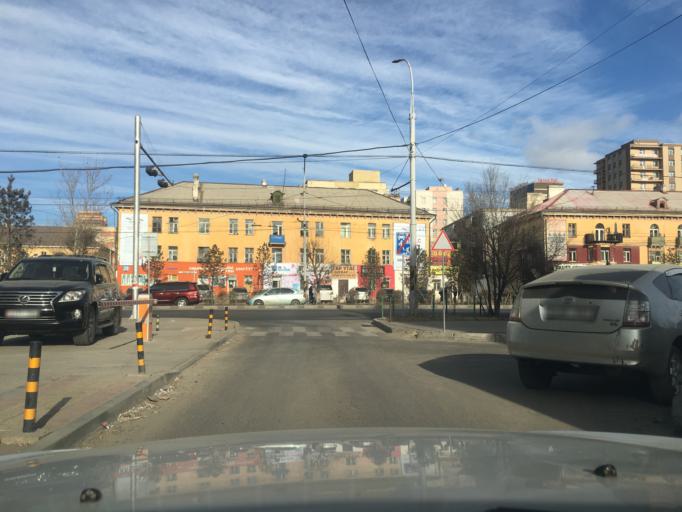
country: MN
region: Ulaanbaatar
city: Ulaanbaatar
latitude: 47.9142
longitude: 106.8813
